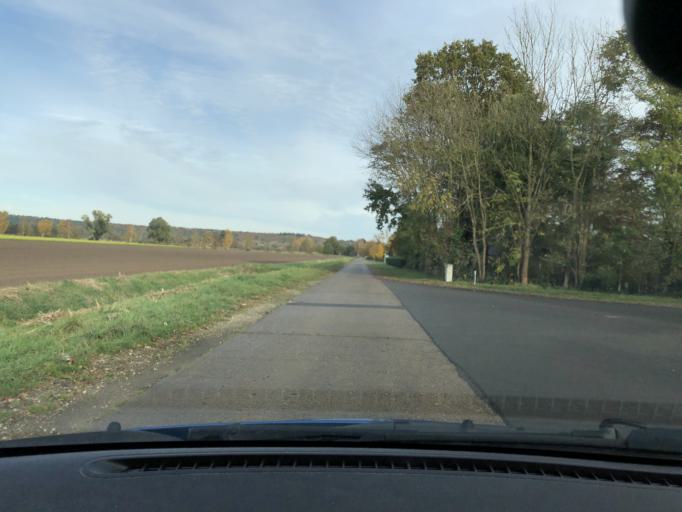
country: DE
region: Lower Saxony
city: Artlenburg
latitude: 53.3674
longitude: 10.4741
